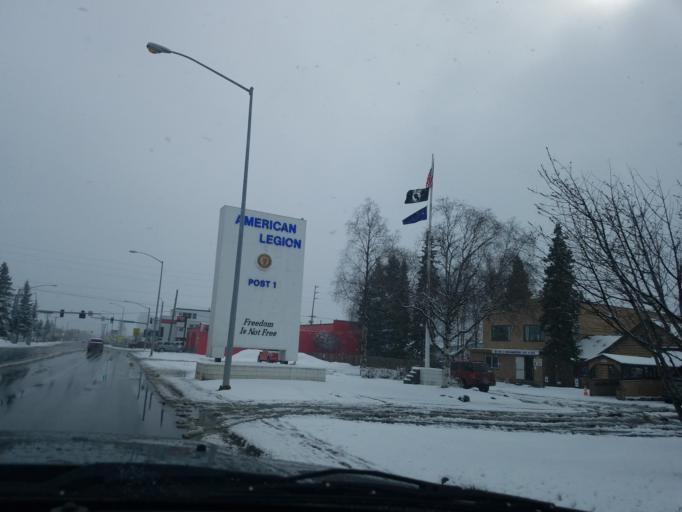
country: US
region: Alaska
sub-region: Anchorage Municipality
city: Anchorage
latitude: 61.1987
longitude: -149.9001
